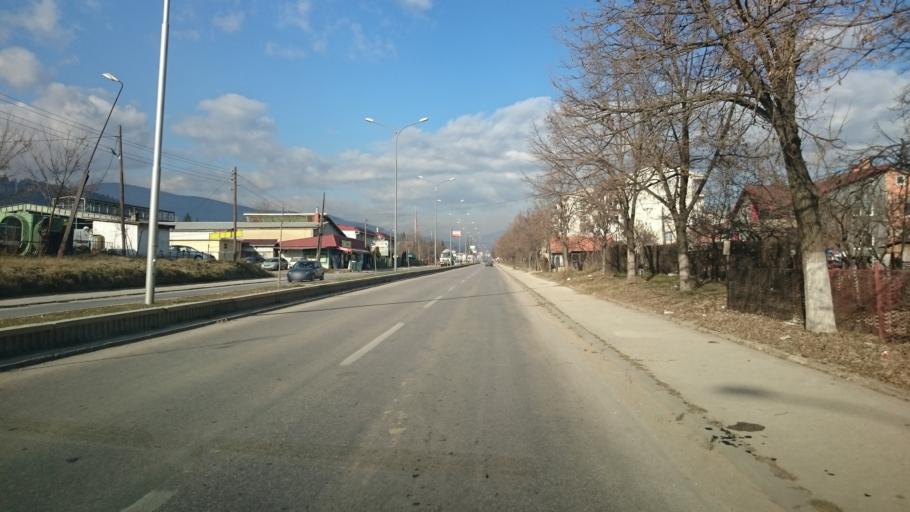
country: MK
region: Kicevo
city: Kicevo
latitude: 41.5092
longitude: 20.9525
